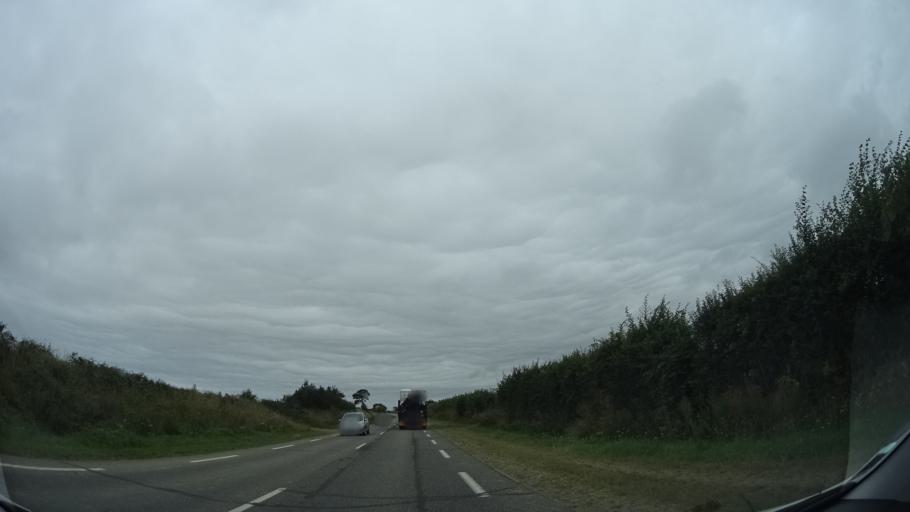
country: FR
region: Lower Normandy
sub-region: Departement de la Manche
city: Portbail
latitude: 49.3653
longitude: -1.7134
